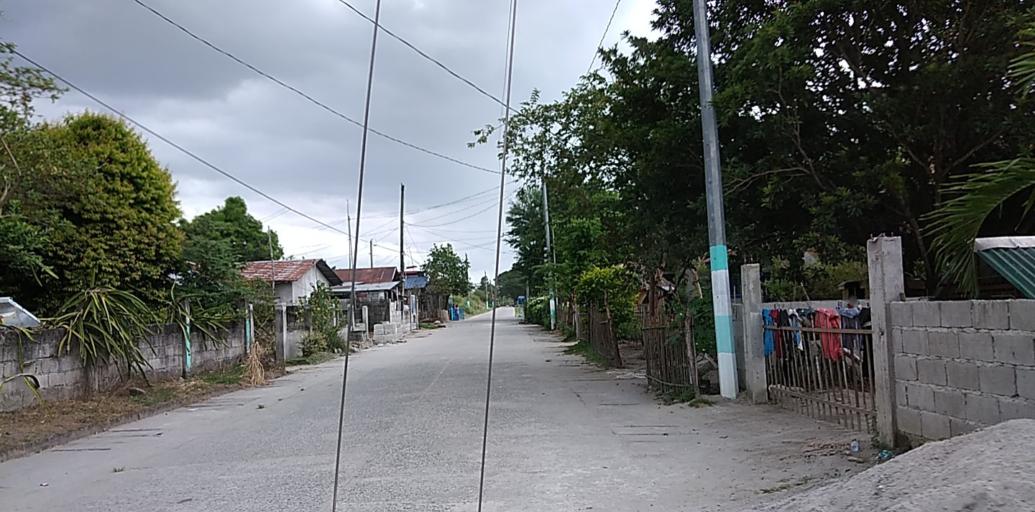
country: PH
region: Central Luzon
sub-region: Province of Pampanga
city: Pio
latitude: 15.0484
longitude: 120.5382
